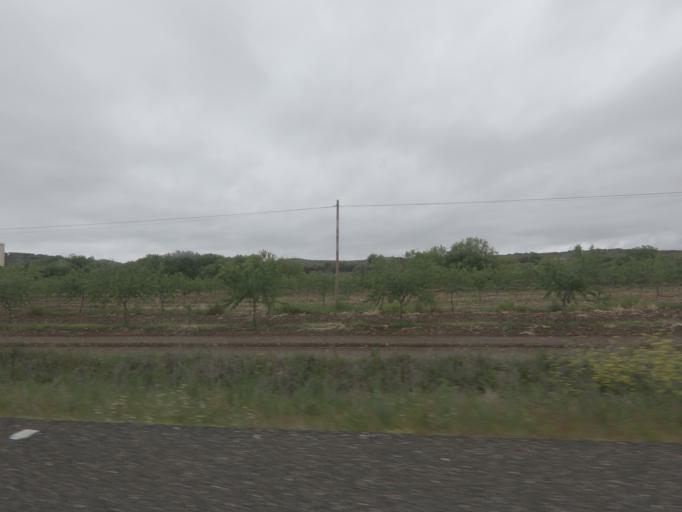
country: ES
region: Extremadura
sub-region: Provincia de Badajoz
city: La Roca de la Sierra
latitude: 39.1182
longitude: -6.6790
